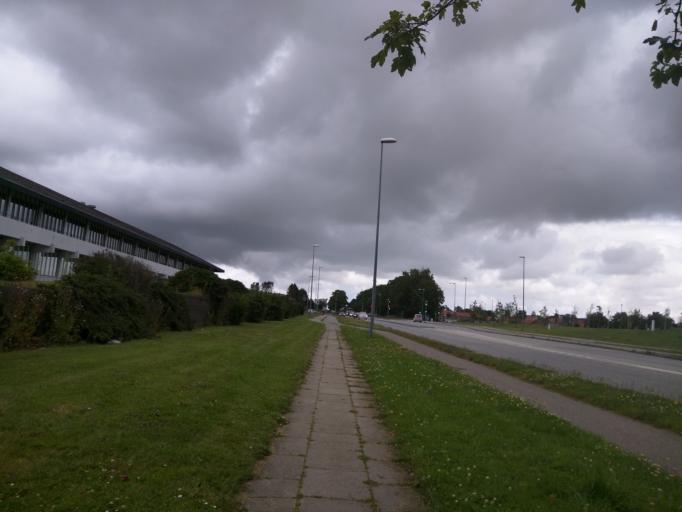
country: DK
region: Central Jutland
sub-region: Viborg Kommune
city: Viborg
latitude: 56.4589
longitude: 9.3973
